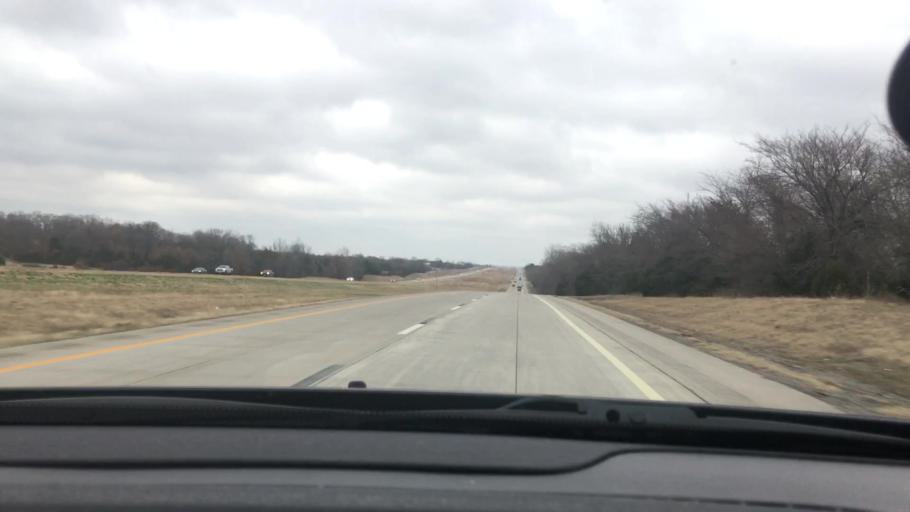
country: US
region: Oklahoma
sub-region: Bryan County
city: Durant
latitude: 34.1782
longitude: -96.2489
